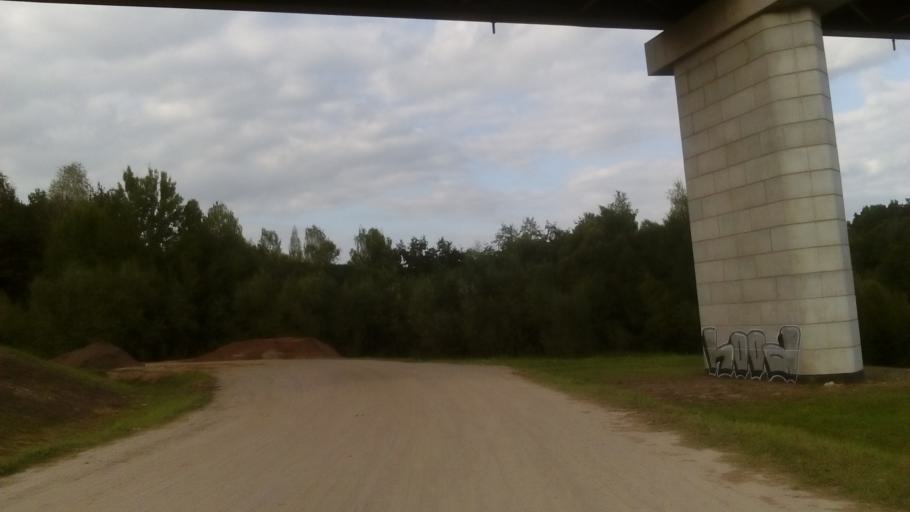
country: LT
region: Alytaus apskritis
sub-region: Alytus
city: Alytus
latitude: 54.4211
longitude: 24.0390
